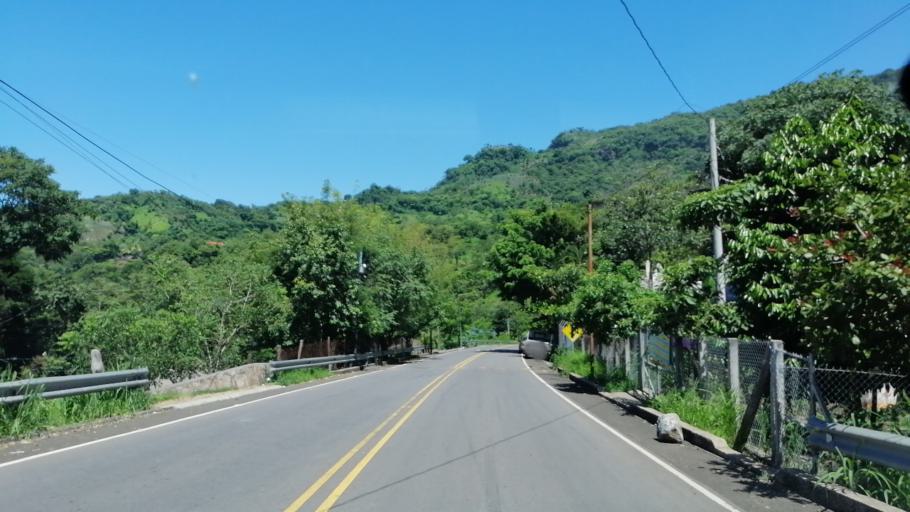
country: SV
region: San Miguel
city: Ciudad Barrios
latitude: 13.8141
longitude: -88.1843
